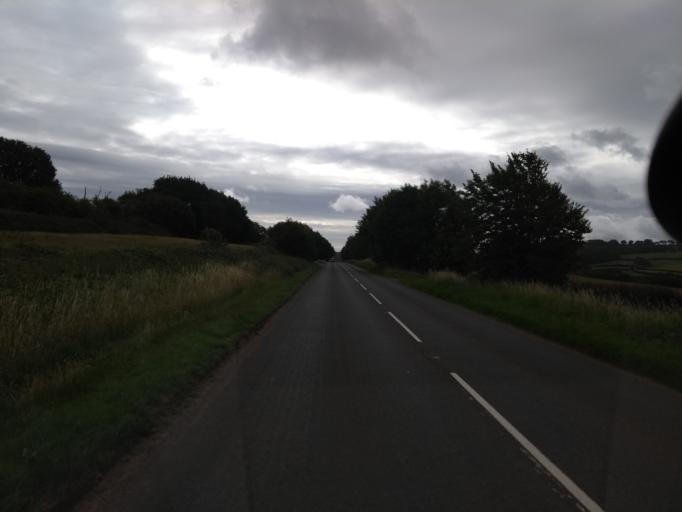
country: GB
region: England
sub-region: Somerset
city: Wiveliscombe
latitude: 51.0405
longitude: -3.2924
